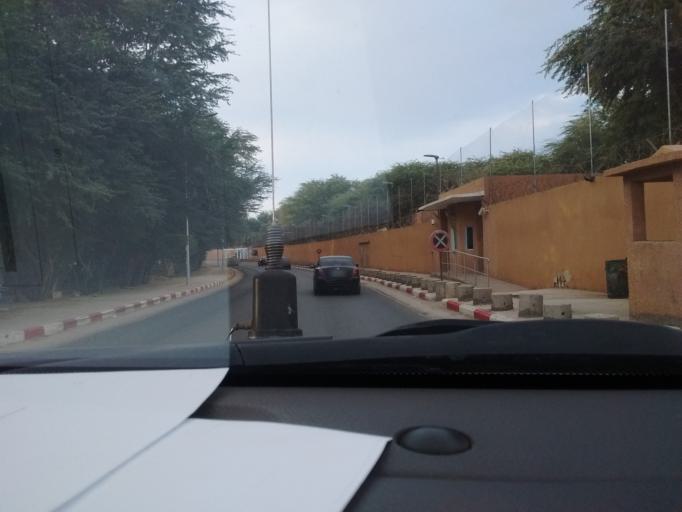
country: MR
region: Nouakchott
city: Nouakchott
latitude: 18.0946
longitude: -15.9823
